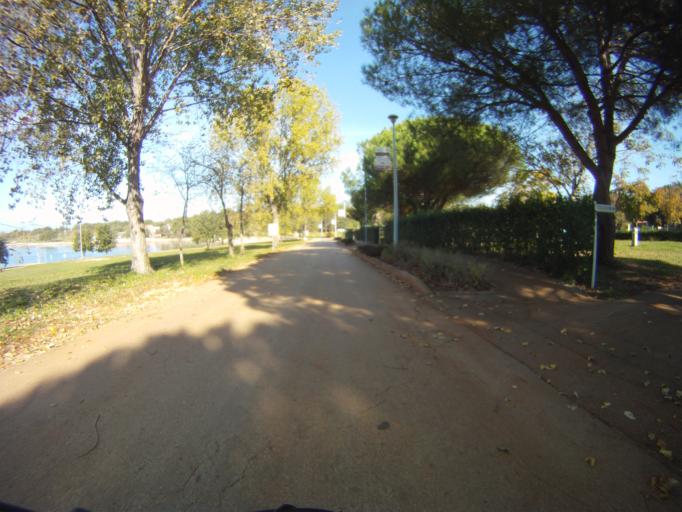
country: HR
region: Istarska
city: Novigrad
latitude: 45.3710
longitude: 13.5455
